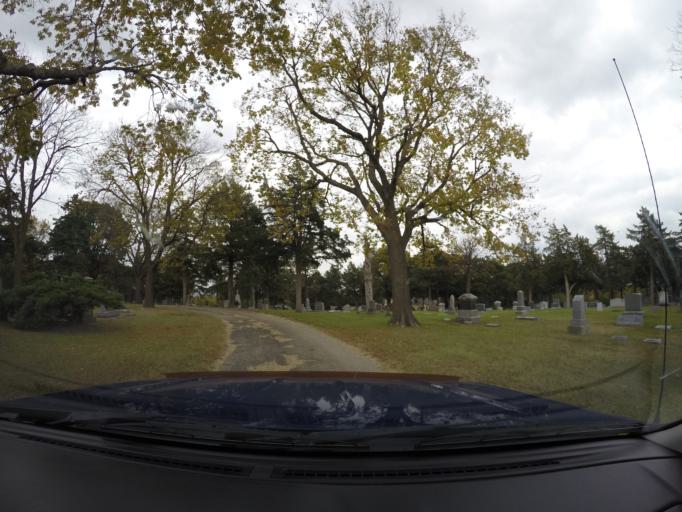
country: US
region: Kansas
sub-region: Geary County
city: Junction City
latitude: 39.0126
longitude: -96.8414
